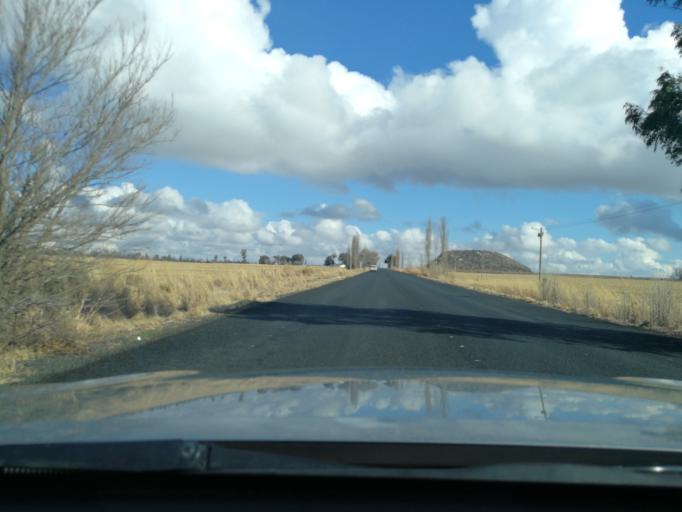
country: ZA
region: Orange Free State
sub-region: Thabo Mofutsanyana District Municipality
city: Reitz
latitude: -27.8881
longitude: 28.3978
